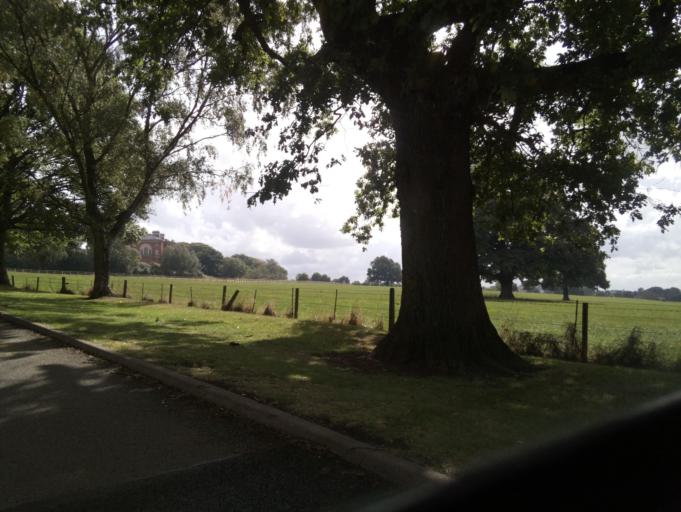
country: GB
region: England
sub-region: Staffordshire
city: Barlaston
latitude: 52.9514
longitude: -2.1602
